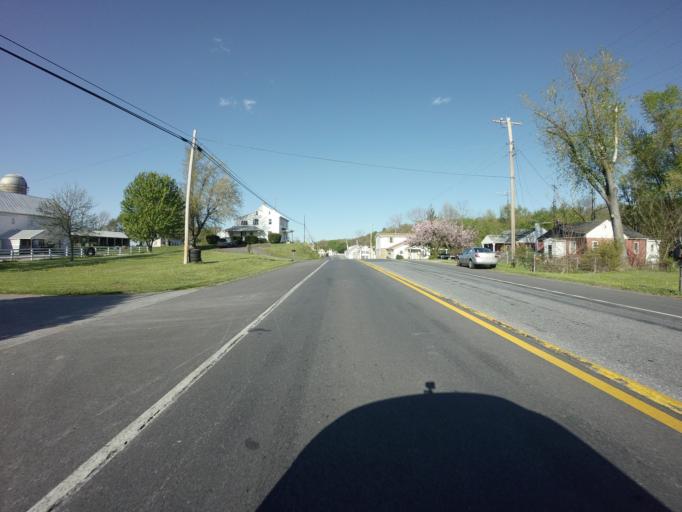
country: US
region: Maryland
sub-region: Frederick County
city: Woodsboro
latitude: 39.5758
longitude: -77.2669
